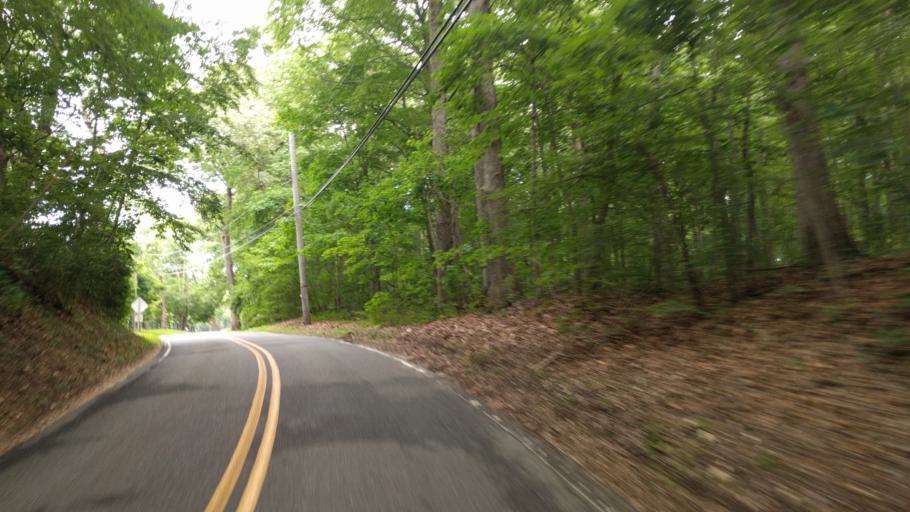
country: US
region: New York
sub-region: Nassau County
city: Oyster Bay Cove
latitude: 40.8603
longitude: -73.5148
